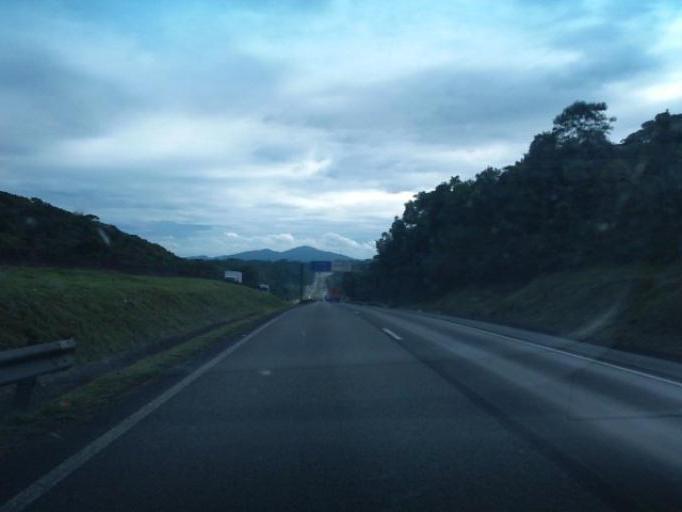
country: BR
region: Parana
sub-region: Campina Grande Do Sul
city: Campina Grande do Sul
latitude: -25.2714
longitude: -48.9202
